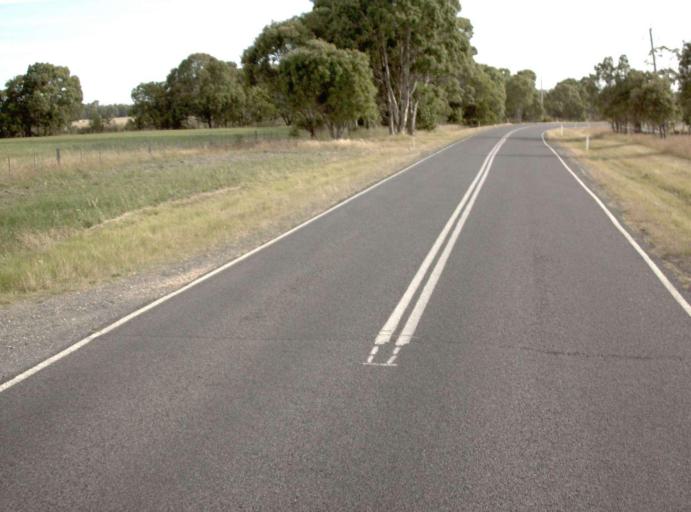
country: AU
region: Victoria
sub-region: Wellington
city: Heyfield
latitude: -38.0559
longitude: 146.6627
